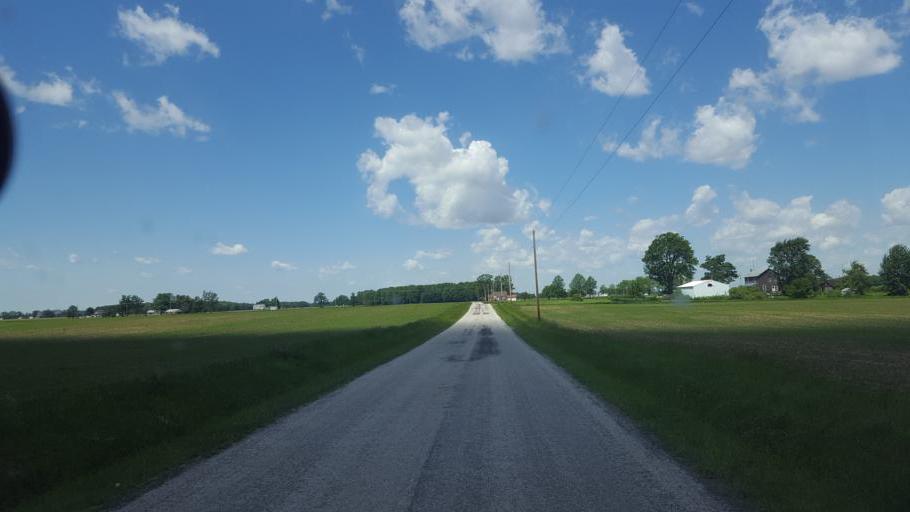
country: US
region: Ohio
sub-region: Richland County
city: Shelby
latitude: 40.8525
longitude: -82.7144
